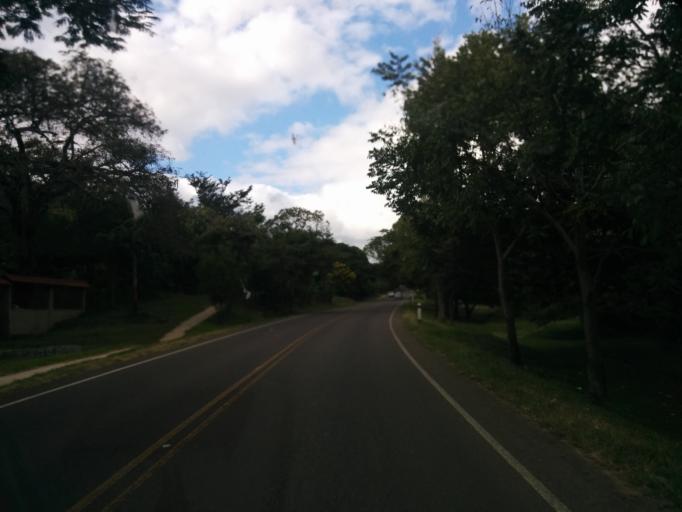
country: NI
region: Esteli
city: Esteli
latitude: 13.0046
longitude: -86.3085
